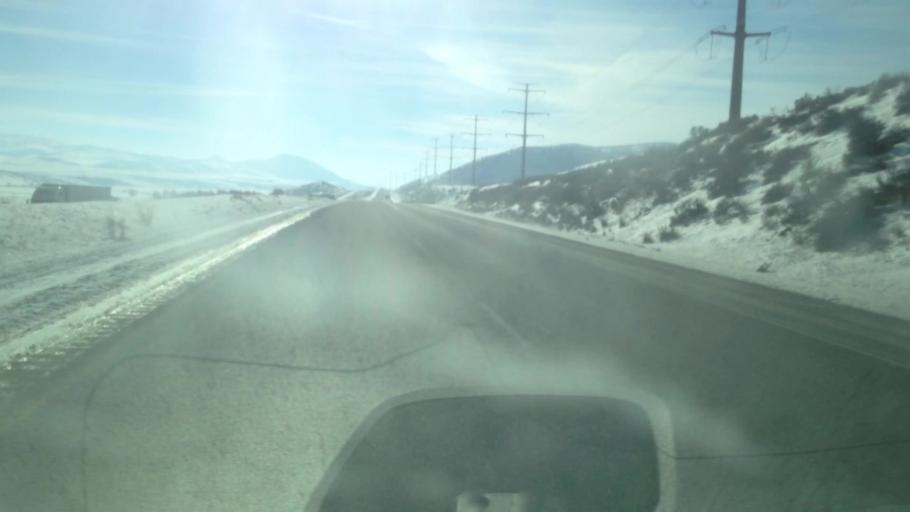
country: US
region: Idaho
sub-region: Oneida County
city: Malad City
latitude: 42.2754
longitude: -112.2131
